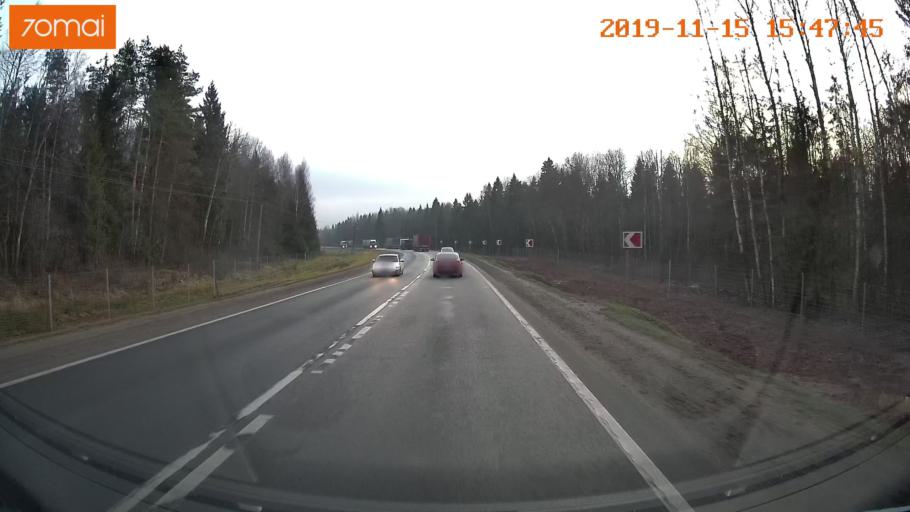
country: RU
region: Jaroslavl
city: Danilov
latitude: 57.9349
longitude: 40.0072
